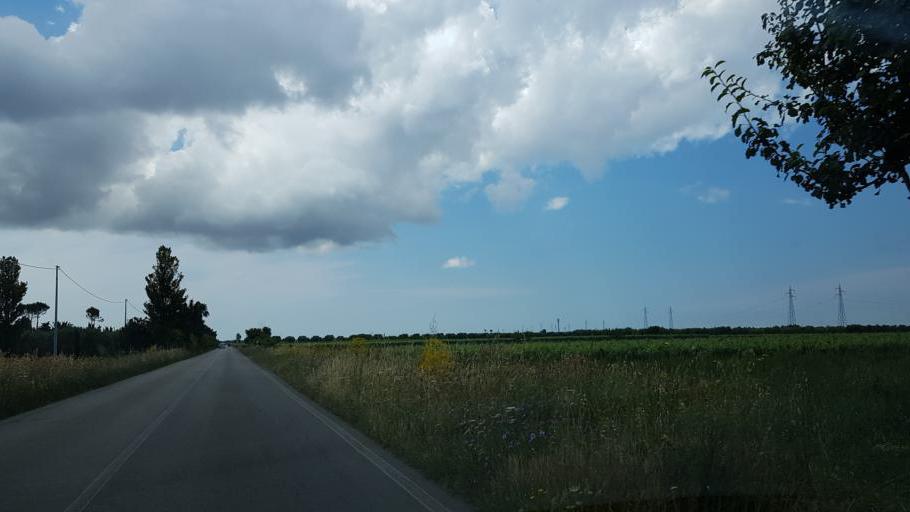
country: IT
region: Apulia
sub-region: Provincia di Brindisi
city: San Pancrazio Salentino
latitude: 40.3891
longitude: 17.8356
